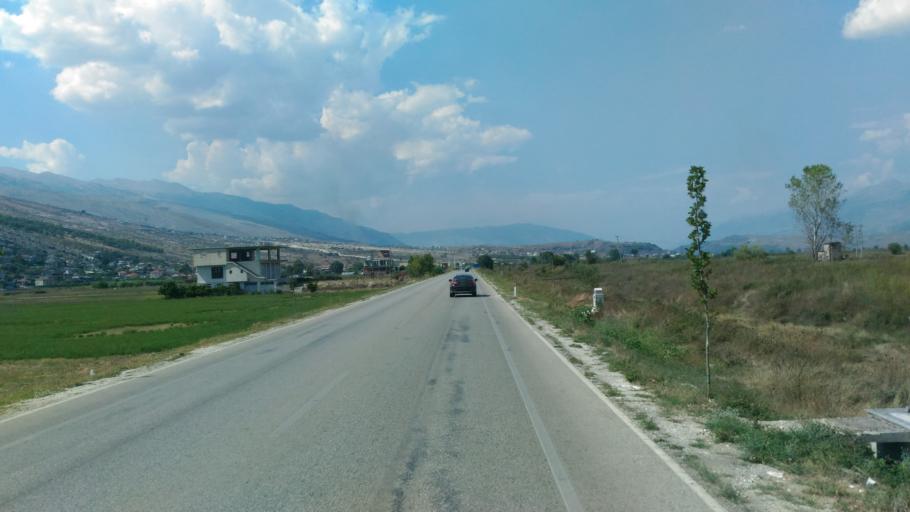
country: AL
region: Gjirokaster
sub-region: Rrethi i Gjirokastres
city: Dervician
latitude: 40.0263
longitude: 20.1889
